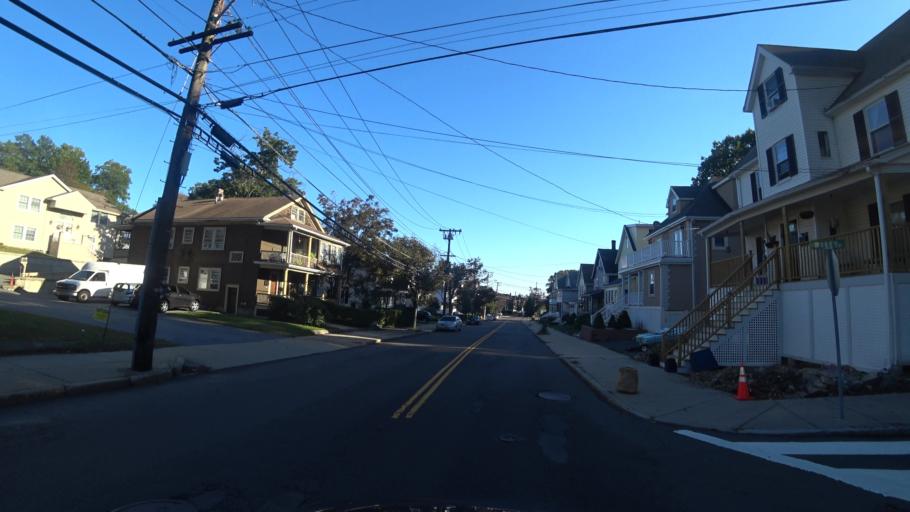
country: US
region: Massachusetts
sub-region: Middlesex County
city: Malden
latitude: 42.4332
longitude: -71.0823
